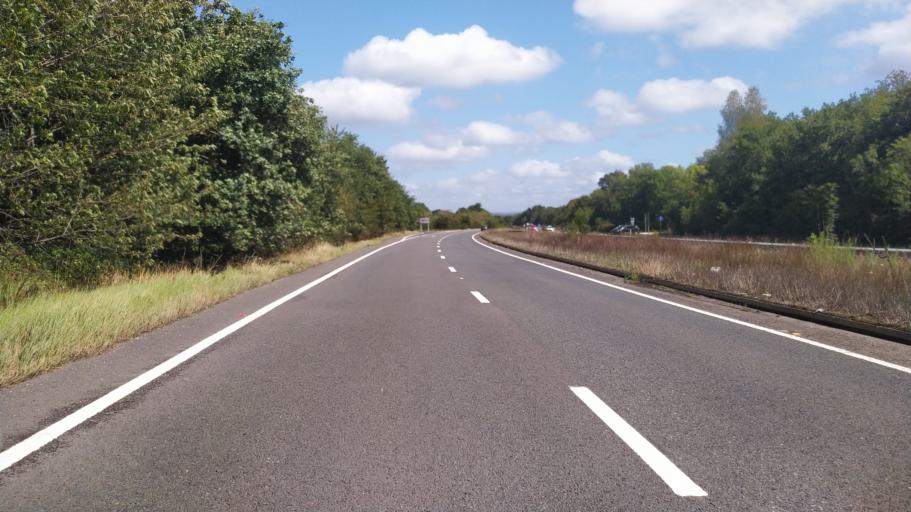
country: GB
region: England
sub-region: Hampshire
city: Petersfield
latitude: 51.0272
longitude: -0.9168
